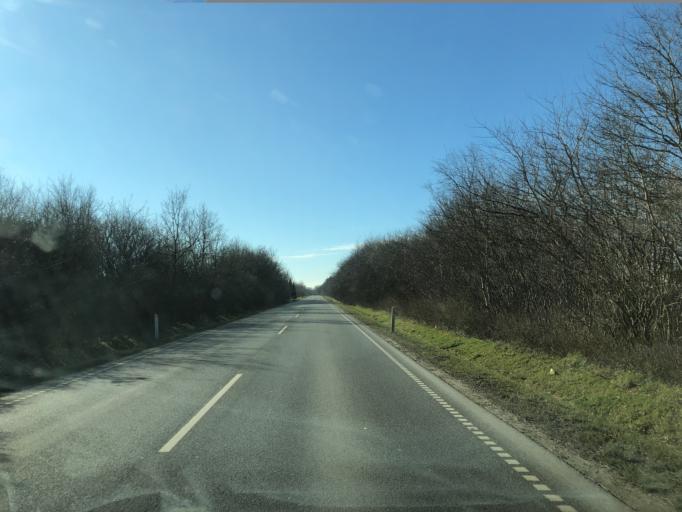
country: DK
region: Central Jutland
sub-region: Ikast-Brande Kommune
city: Bording Kirkeby
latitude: 56.1480
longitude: 9.2223
